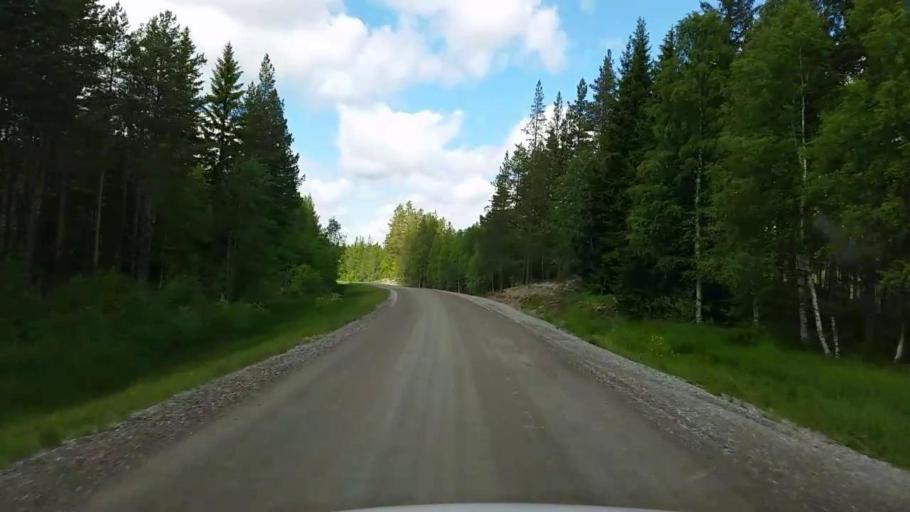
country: SE
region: Gaevleborg
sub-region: Bollnas Kommun
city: Vittsjo
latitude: 61.0582
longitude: 16.3227
